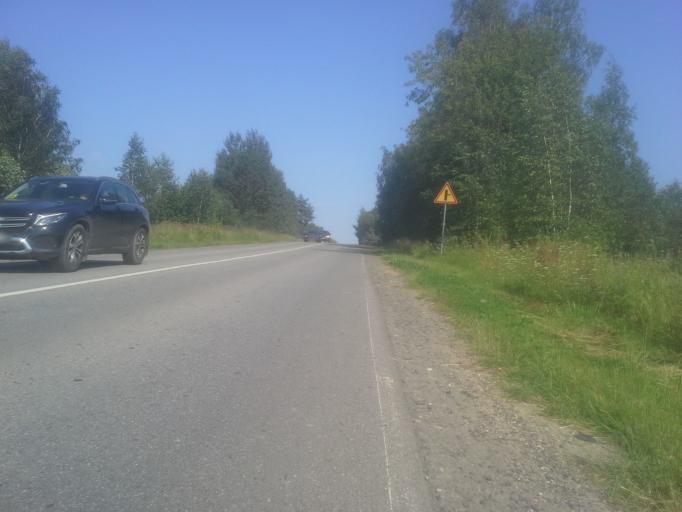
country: RU
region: Moskovskaya
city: Kolyubakino
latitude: 55.6409
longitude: 36.5888
